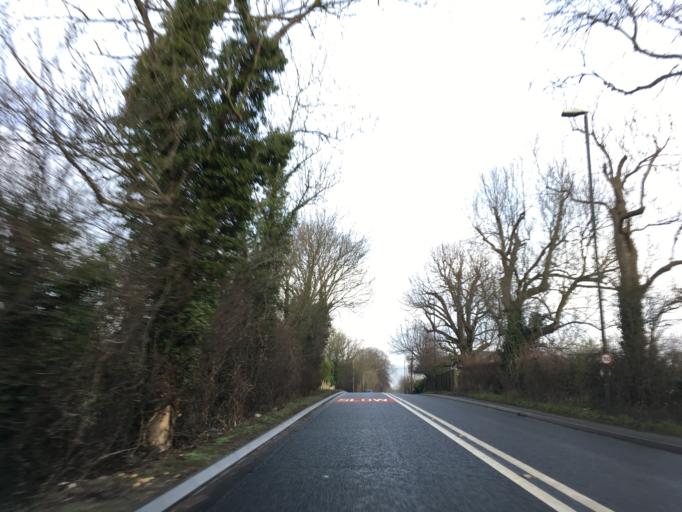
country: GB
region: England
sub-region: Gloucestershire
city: Shurdington
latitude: 51.8536
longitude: -2.1333
